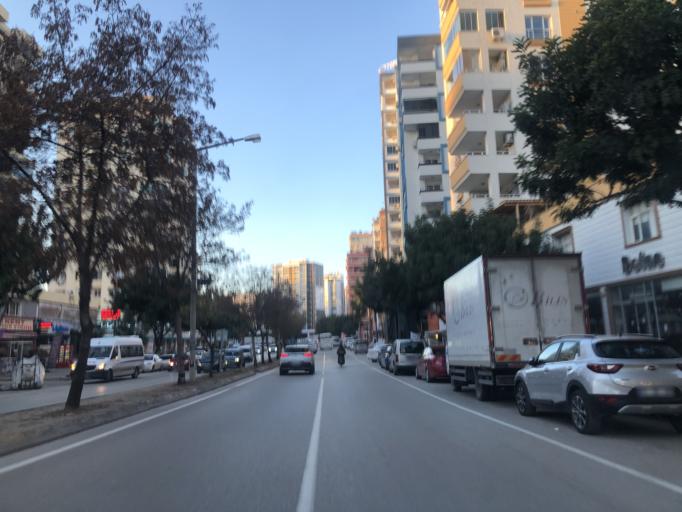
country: TR
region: Adana
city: Adana
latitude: 37.0338
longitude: 35.2994
